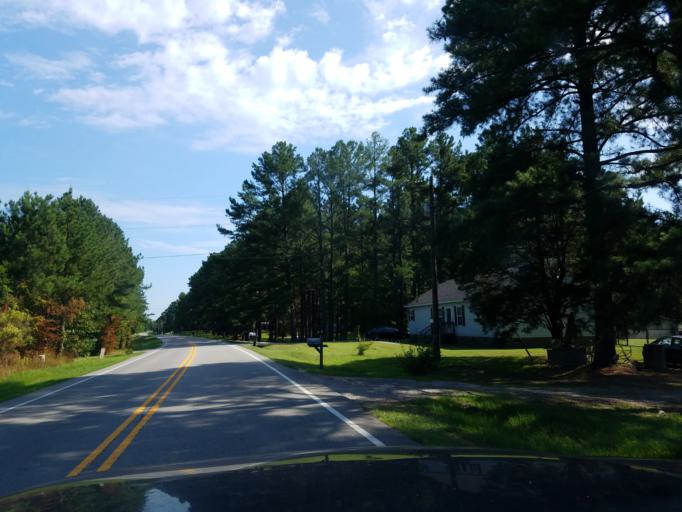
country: US
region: North Carolina
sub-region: Vance County
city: Henderson
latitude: 36.3632
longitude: -78.4188
